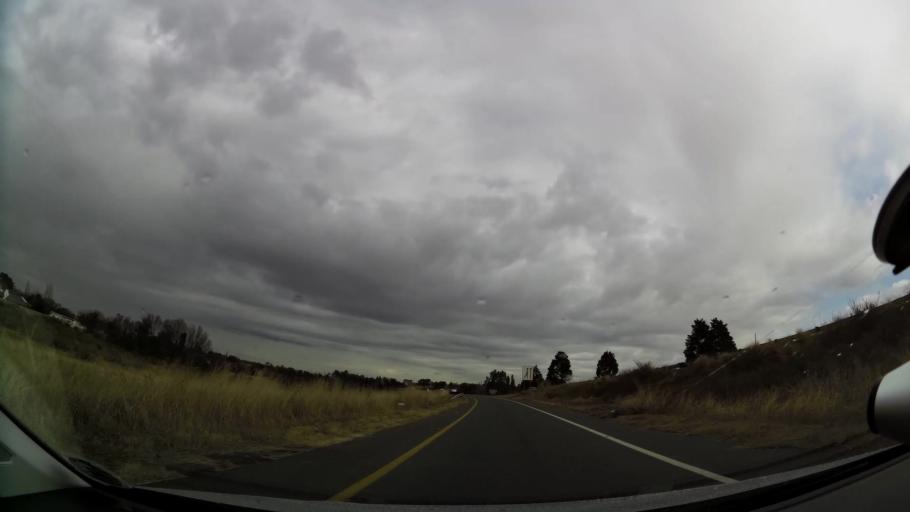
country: ZA
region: Orange Free State
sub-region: Fezile Dabi District Municipality
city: Kroonstad
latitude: -27.6582
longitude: 27.2510
